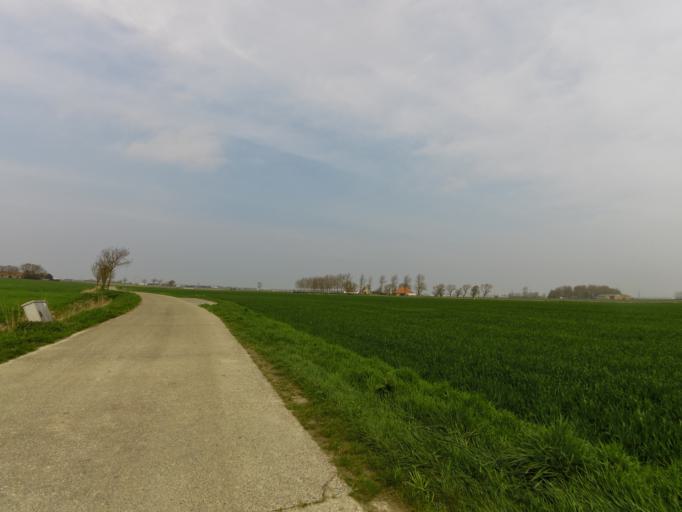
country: BE
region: Flanders
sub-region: Provincie West-Vlaanderen
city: Middelkerke
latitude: 51.1819
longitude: 2.8594
